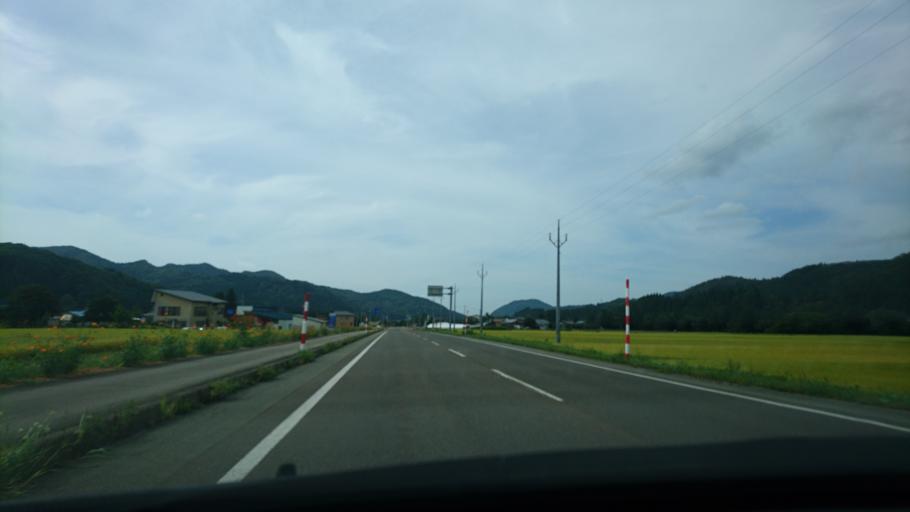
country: JP
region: Akita
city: Yuzawa
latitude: 39.1833
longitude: 140.6427
